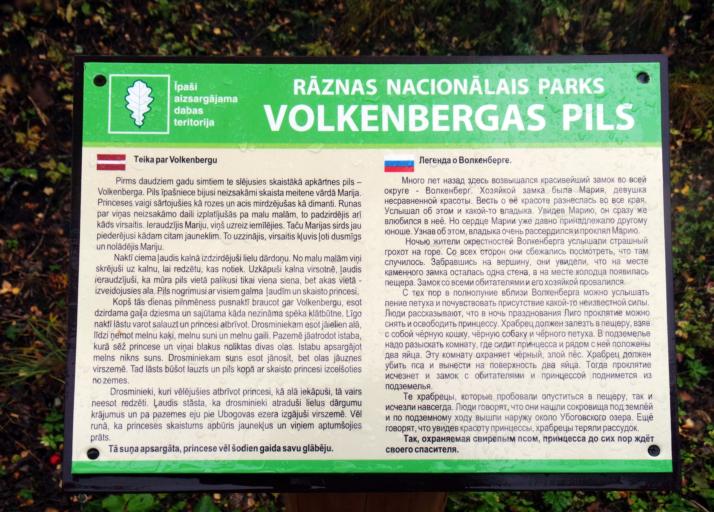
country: LV
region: Dagda
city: Dagda
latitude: 56.2776
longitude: 27.4136
